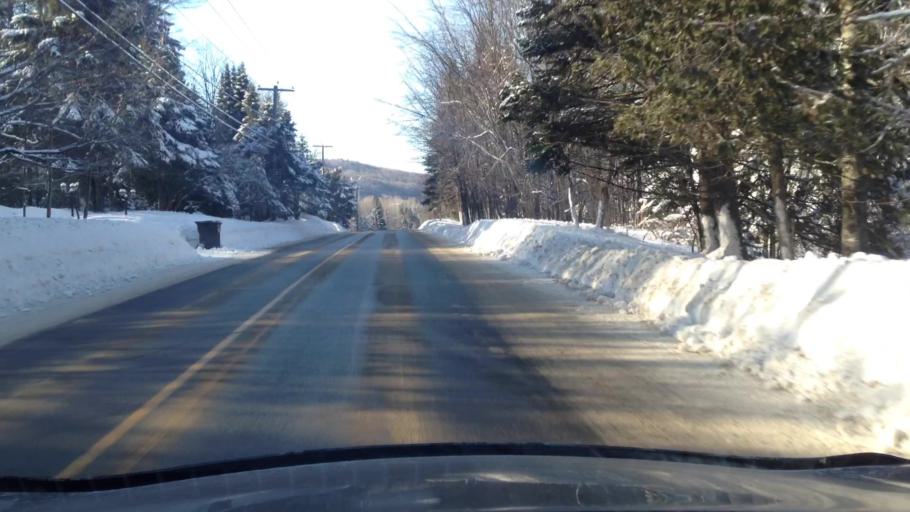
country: CA
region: Quebec
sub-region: Laurentides
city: Sainte-Agathe-des-Monts
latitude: 45.9297
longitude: -74.4116
